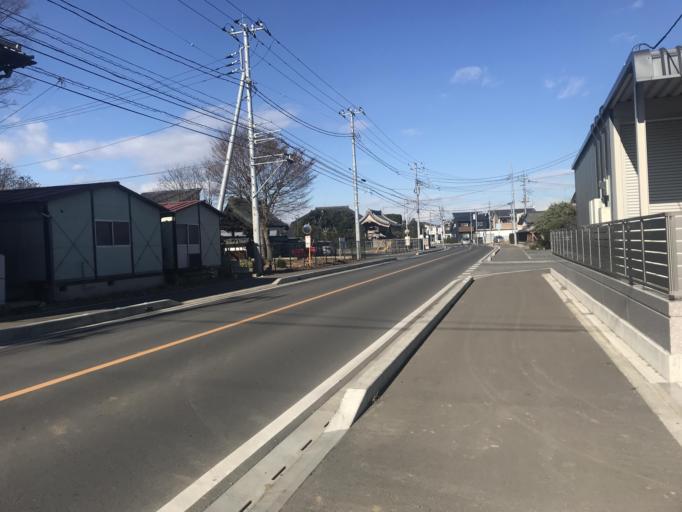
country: JP
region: Tochigi
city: Kaminokawa
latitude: 36.3745
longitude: 139.8789
